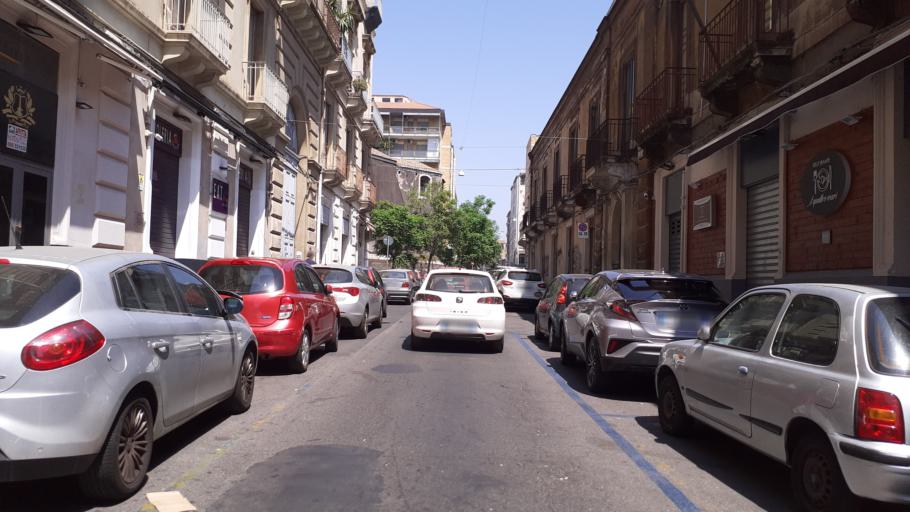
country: IT
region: Sicily
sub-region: Catania
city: Catania
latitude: 37.5058
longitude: 15.0889
